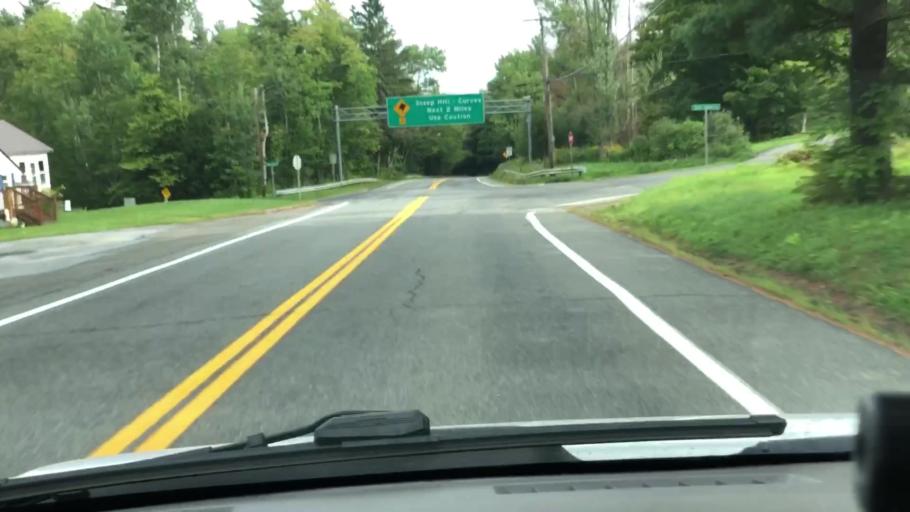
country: US
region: Massachusetts
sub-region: Berkshire County
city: North Adams
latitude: 42.6523
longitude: -72.9980
